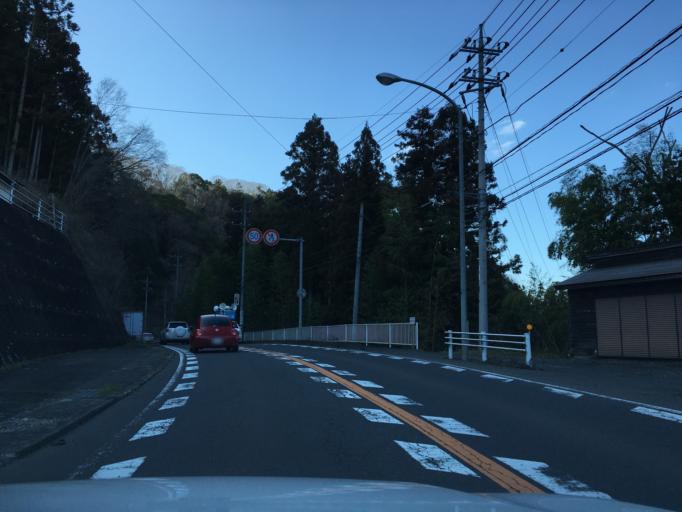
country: JP
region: Ibaraki
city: Daigo
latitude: 36.7511
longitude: 140.3840
